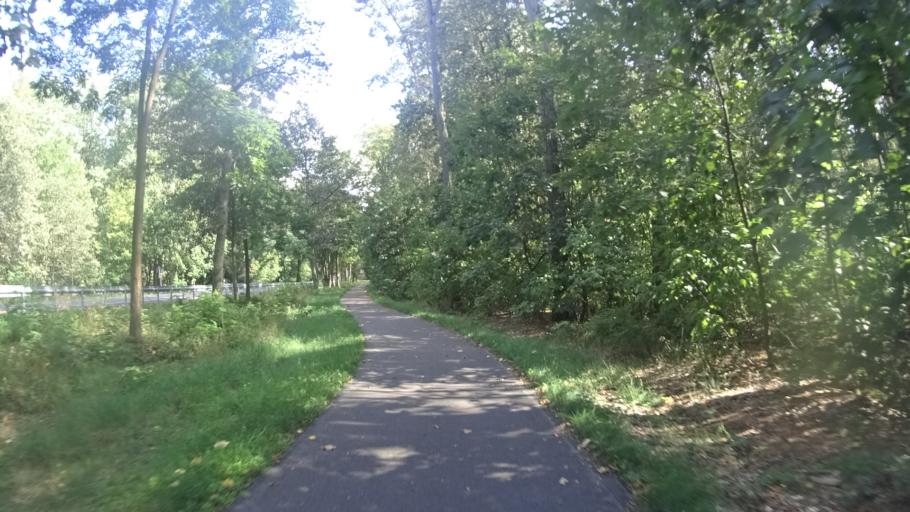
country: DE
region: Brandenburg
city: Rhinow
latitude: 52.7232
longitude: 12.3596
